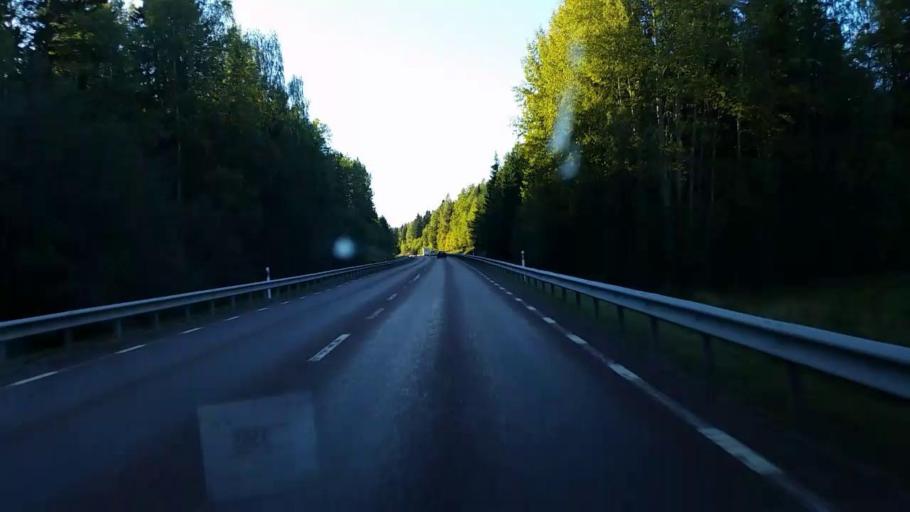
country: SE
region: Gaevleborg
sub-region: Hudiksvalls Kommun
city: Delsbo
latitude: 61.8066
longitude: 16.4337
